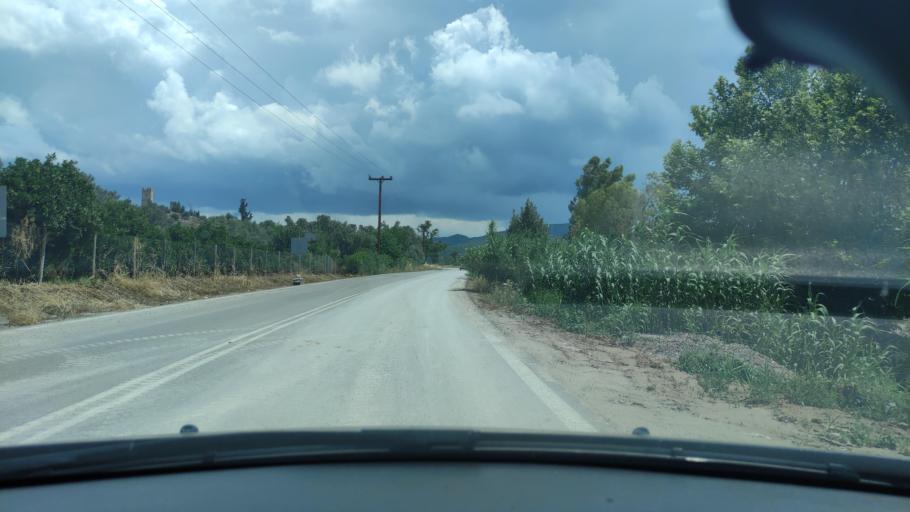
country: GR
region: Central Greece
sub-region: Nomos Evvoias
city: Vasilikon
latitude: 38.4391
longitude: 23.6671
